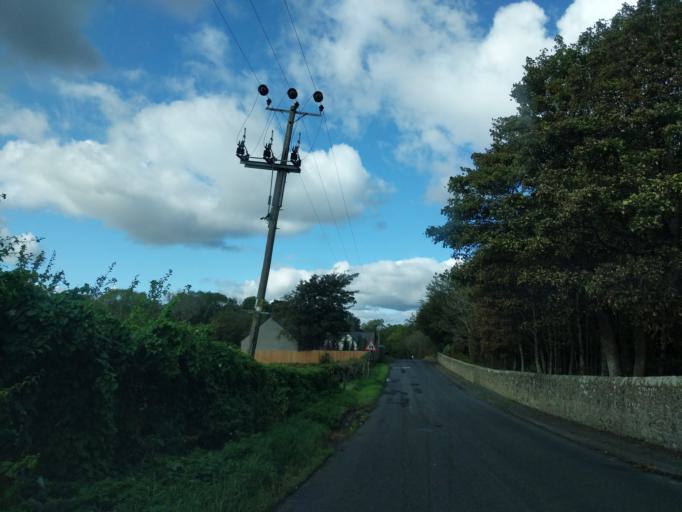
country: GB
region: Scotland
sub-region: Edinburgh
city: Currie
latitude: 55.9084
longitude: -3.3310
